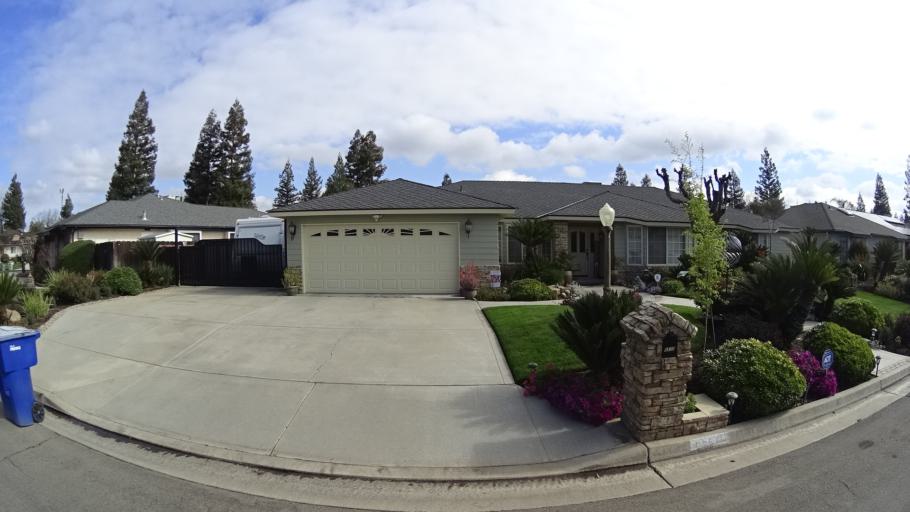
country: US
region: California
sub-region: Fresno County
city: Fresno
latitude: 36.8322
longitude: -119.8596
